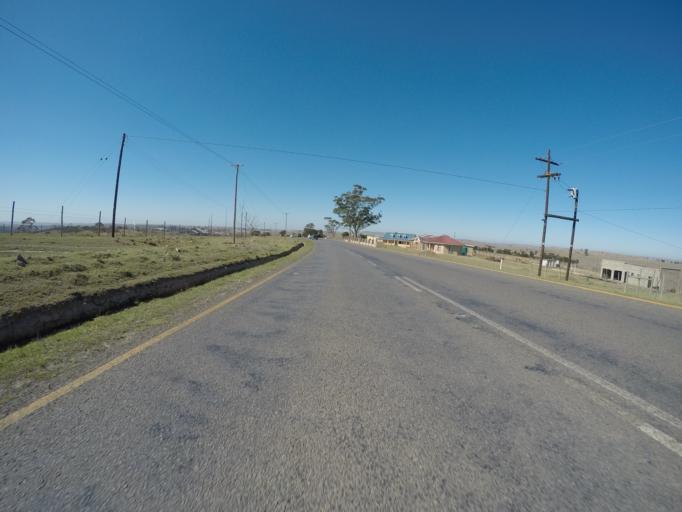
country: ZA
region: Eastern Cape
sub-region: OR Tambo District Municipality
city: Mthatha
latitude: -31.7955
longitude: 28.7449
